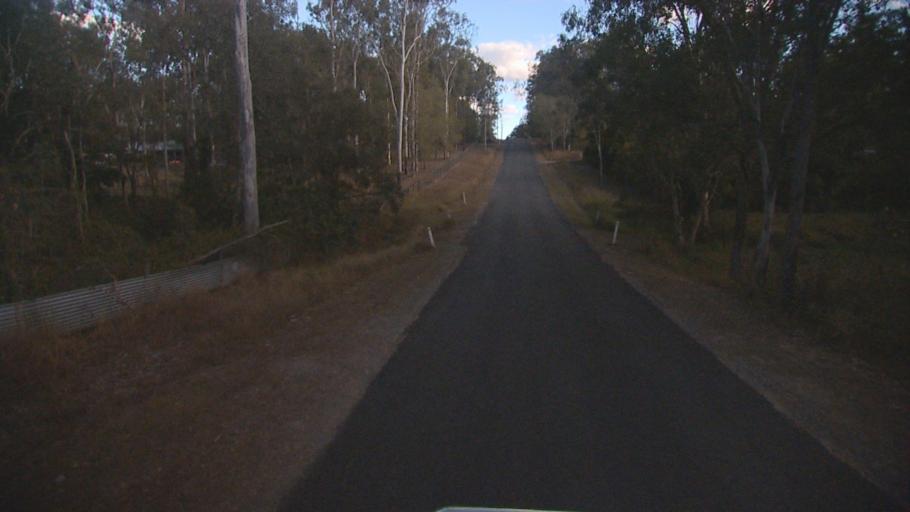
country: AU
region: Queensland
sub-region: Logan
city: Cedar Vale
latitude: -27.8492
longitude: 153.0903
